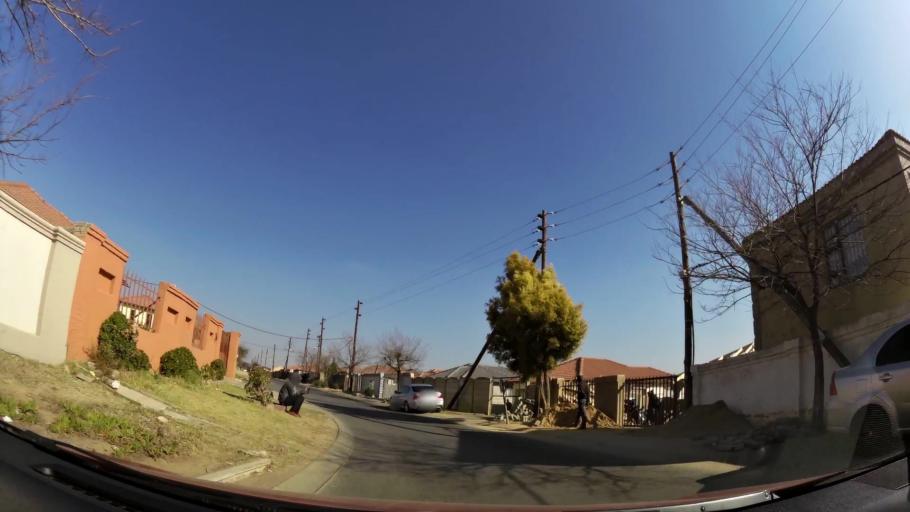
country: ZA
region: Gauteng
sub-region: West Rand District Municipality
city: Muldersdriseloop
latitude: -26.0414
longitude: 27.9197
